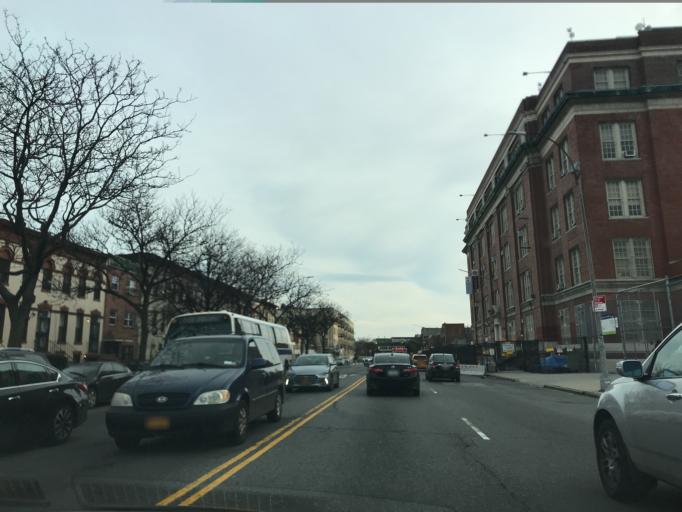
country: US
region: New York
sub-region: Kings County
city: East New York
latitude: 40.6678
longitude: -73.8948
